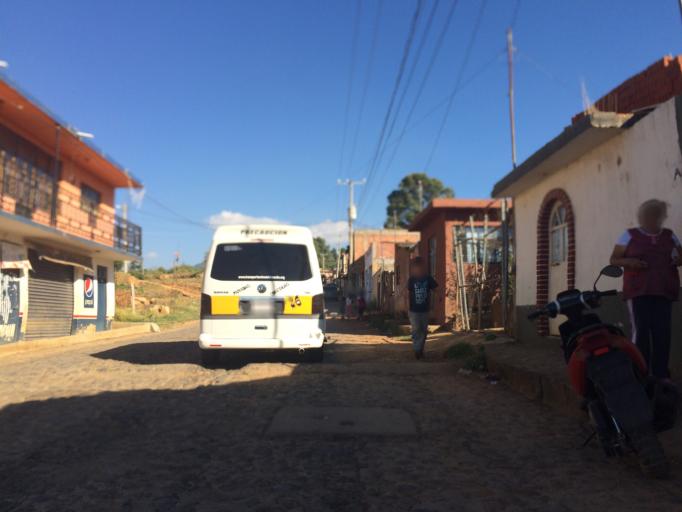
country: MX
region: Michoacan
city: Patzcuaro
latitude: 19.5072
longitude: -101.5975
